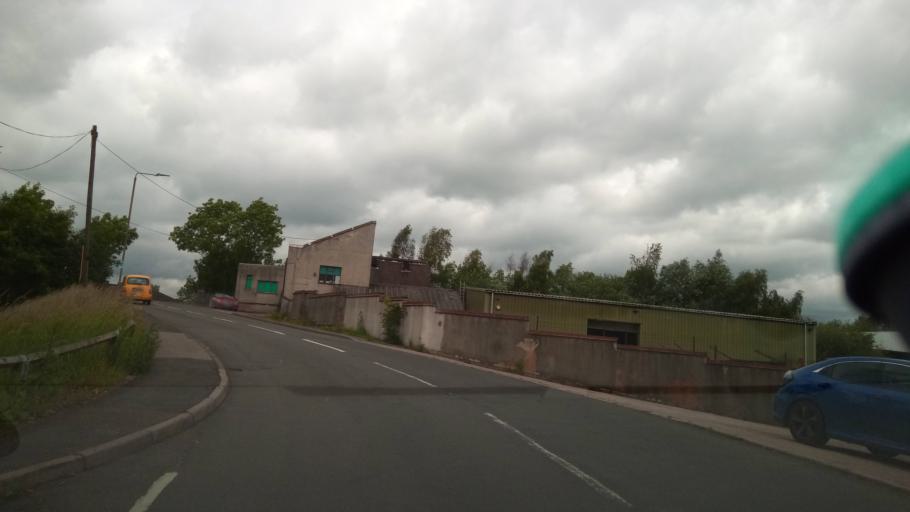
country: GB
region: England
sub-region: Derbyshire
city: Etwall
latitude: 52.8633
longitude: -1.6144
